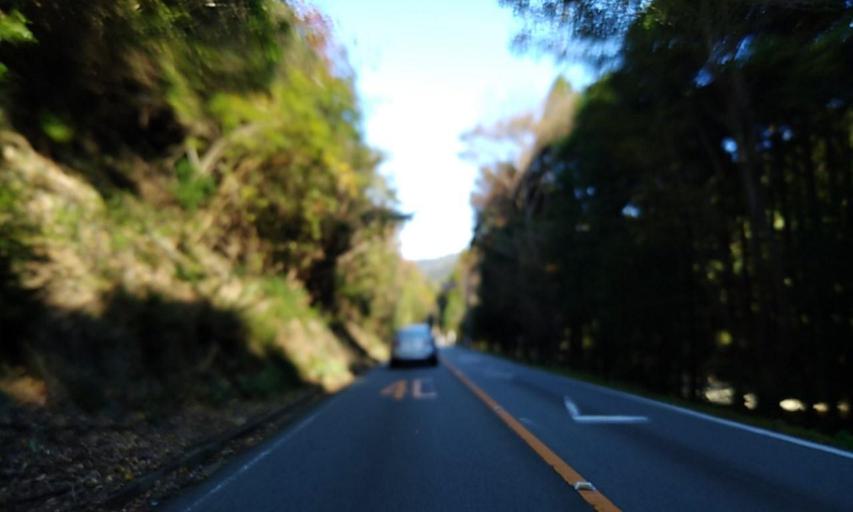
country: JP
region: Mie
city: Ise
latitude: 34.4465
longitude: 136.7503
